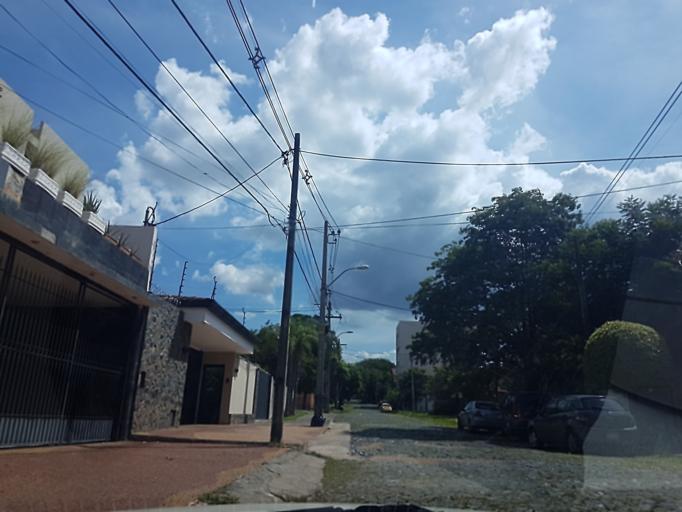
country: PY
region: Asuncion
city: Asuncion
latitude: -25.2728
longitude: -57.5729
